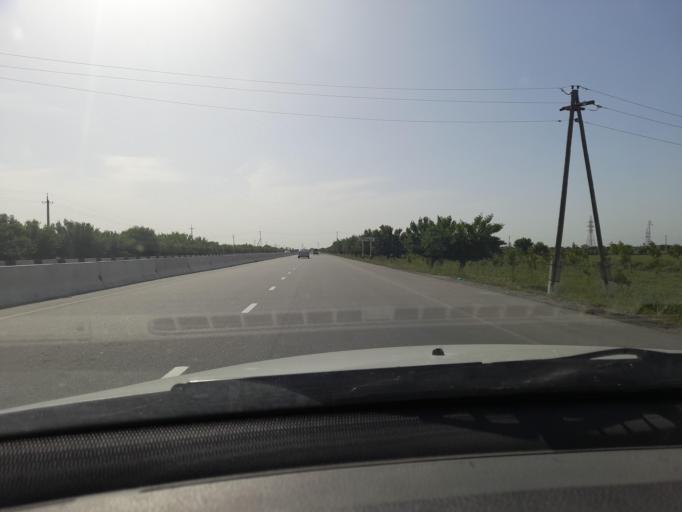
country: UZ
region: Samarqand
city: Ishtixon
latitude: 39.9572
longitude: 66.4730
